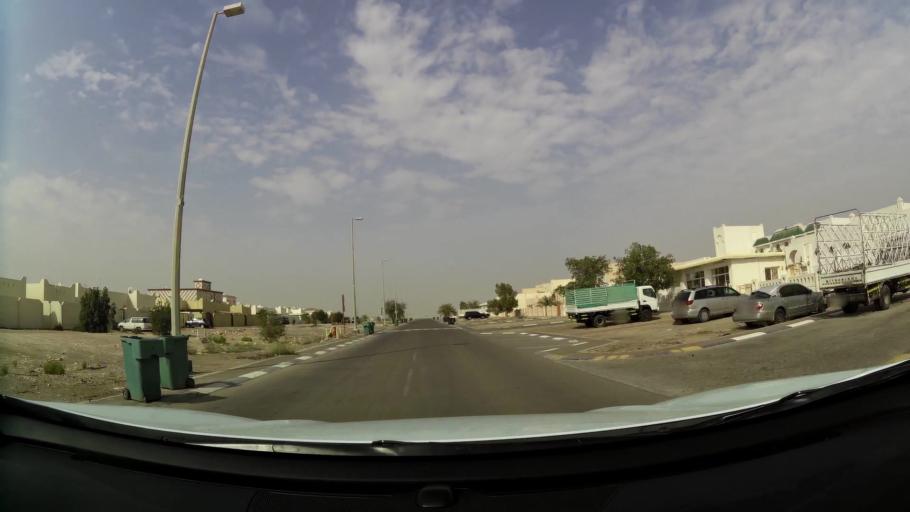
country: AE
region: Abu Dhabi
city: Abu Dhabi
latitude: 24.2789
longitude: 54.6869
